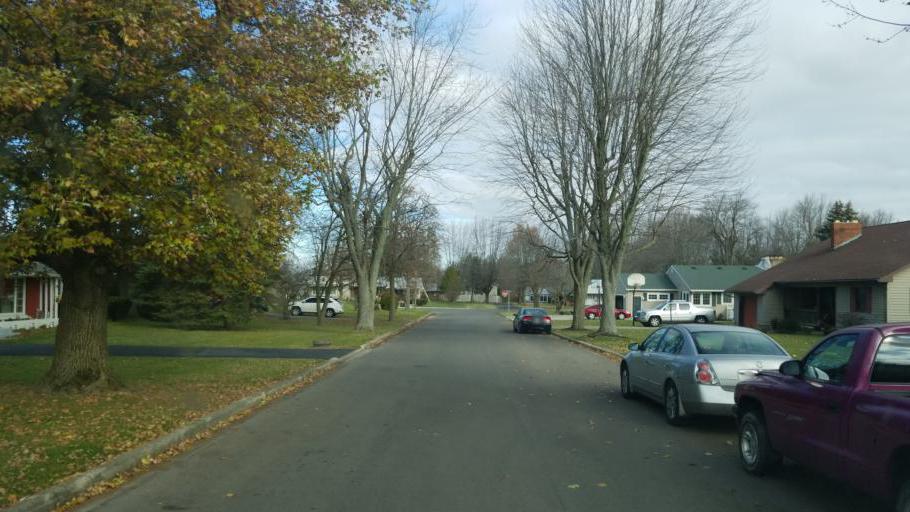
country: US
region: Ohio
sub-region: Hardin County
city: Kenton
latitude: 40.6567
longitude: -83.6040
